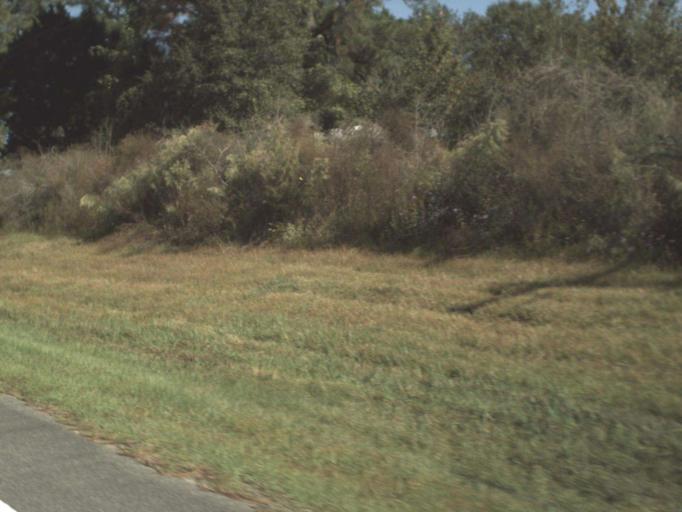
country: US
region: Alabama
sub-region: Geneva County
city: Geneva
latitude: 30.9106
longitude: -85.9581
